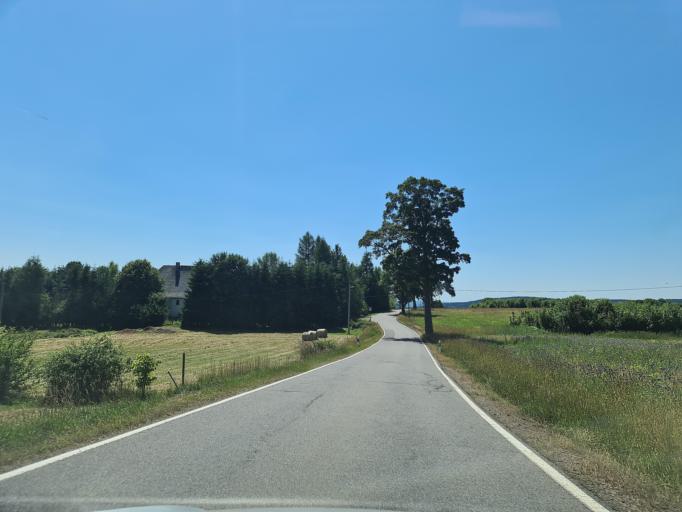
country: DE
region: Saxony
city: Rechenberg-Bienenmuhle
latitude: 50.7177
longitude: 13.5202
